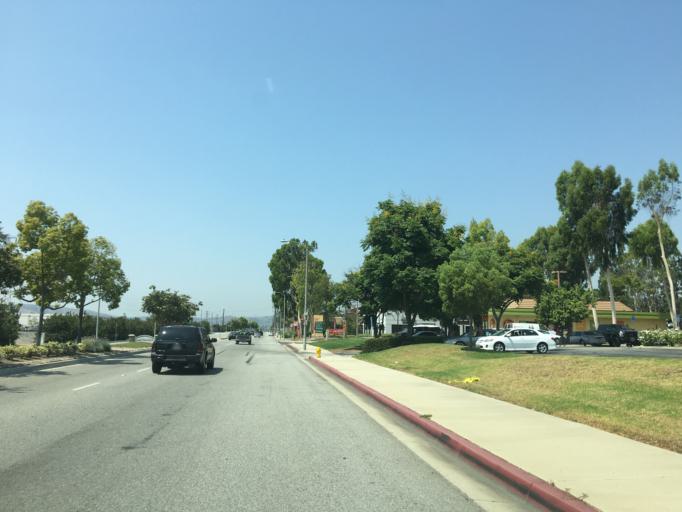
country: US
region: California
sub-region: Los Angeles County
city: Walnut
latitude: 34.0088
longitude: -117.8607
